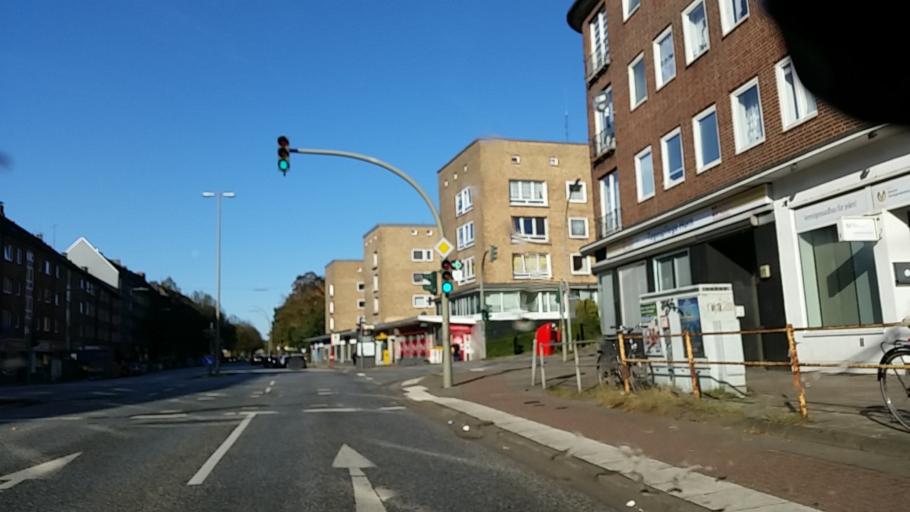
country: DE
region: Hamburg
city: Marienthal
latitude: 53.5502
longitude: 10.0789
